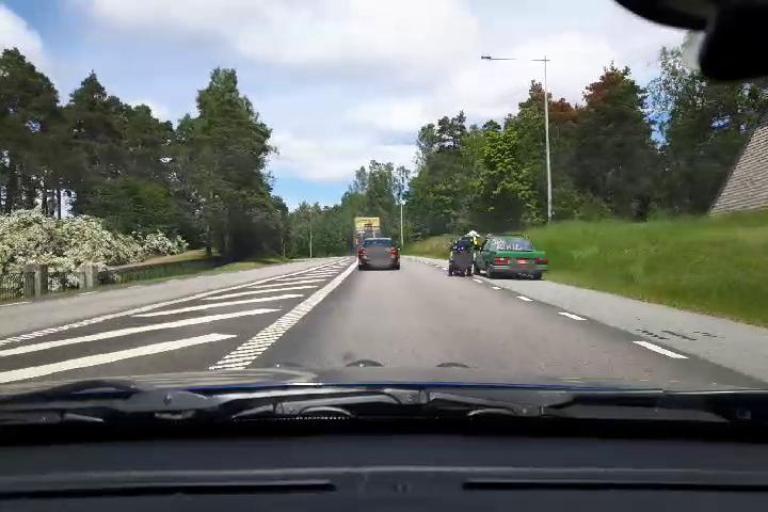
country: SE
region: Uppsala
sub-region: Osthammars Kommun
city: Bjorklinge
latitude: 60.0275
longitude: 17.5534
